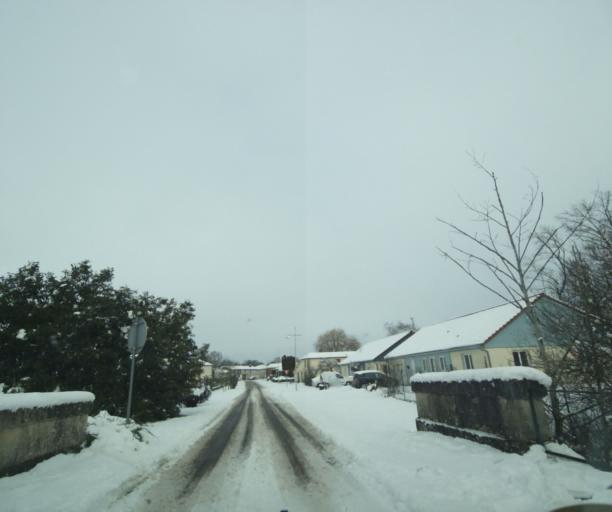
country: FR
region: Champagne-Ardenne
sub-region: Departement de la Haute-Marne
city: Montier-en-Der
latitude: 48.5136
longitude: 4.6992
